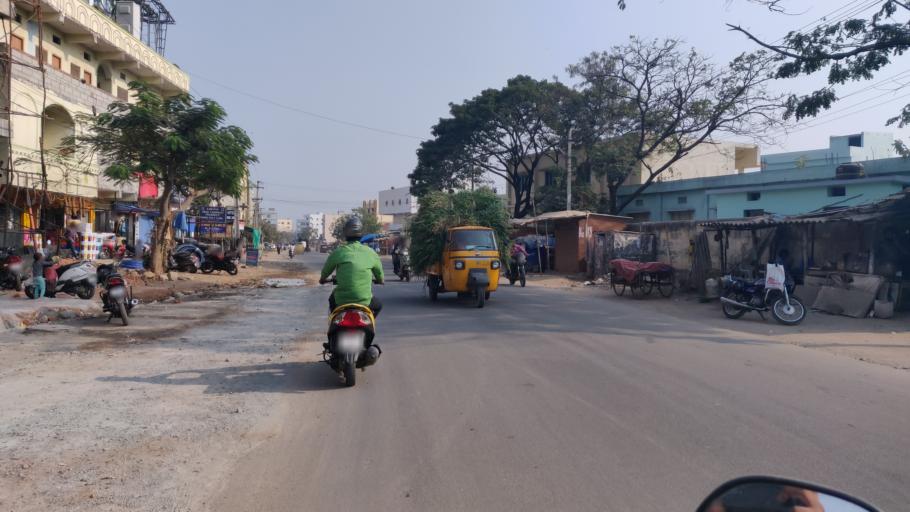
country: IN
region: Telangana
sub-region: Rangareddi
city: Uppal Kalan
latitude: 17.3941
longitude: 78.5946
